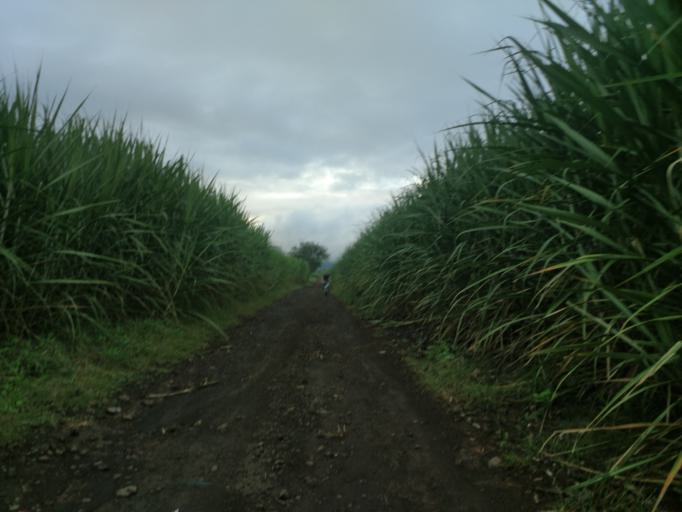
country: MX
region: Nayarit
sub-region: Tepic
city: La Corregidora
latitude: 21.4723
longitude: -104.8041
